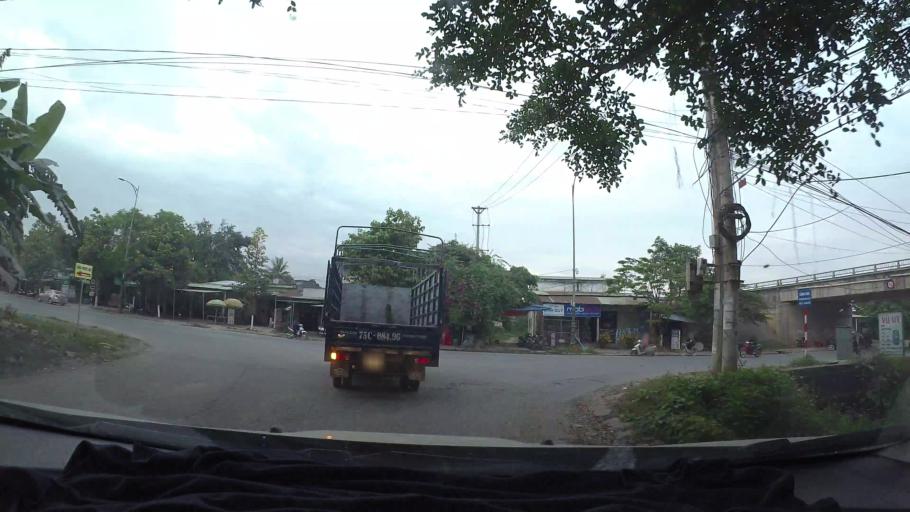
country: VN
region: Da Nang
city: Lien Chieu
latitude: 16.0595
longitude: 108.0974
